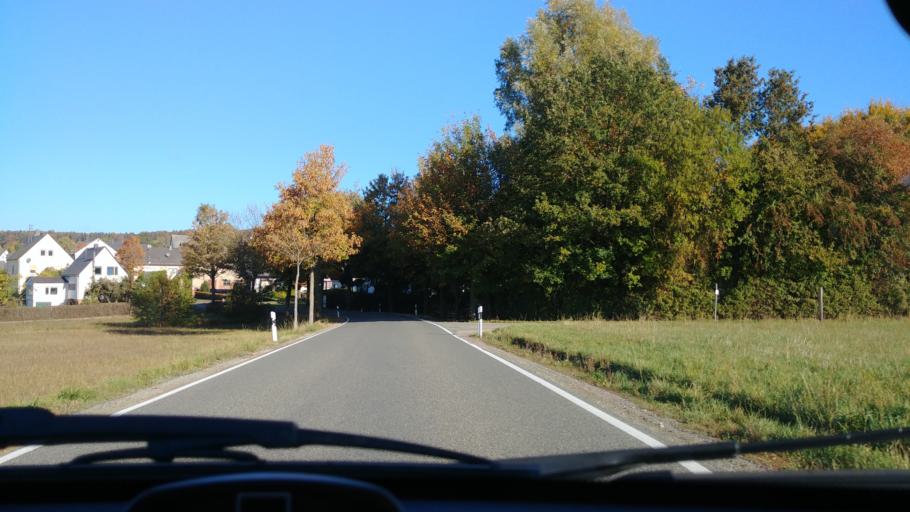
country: DE
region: Rheinland-Pfalz
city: Hunzel
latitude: 50.2457
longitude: 7.8401
